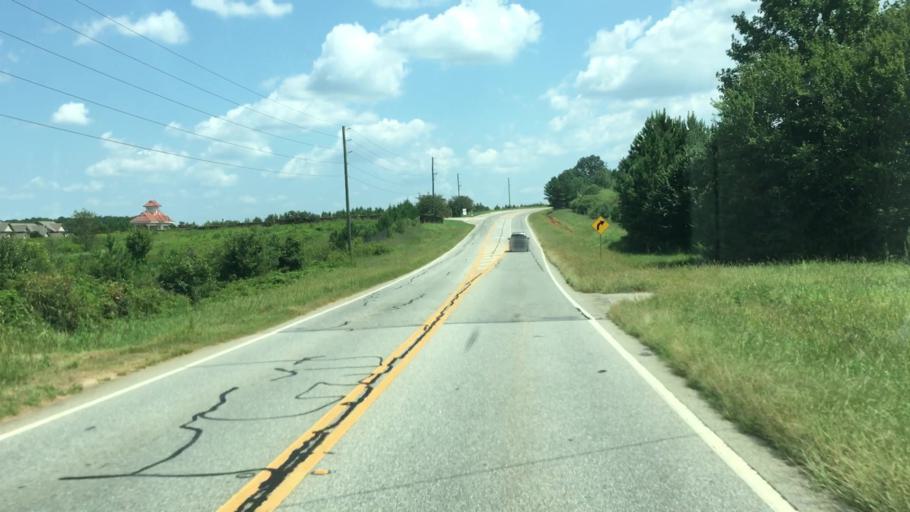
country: US
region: Georgia
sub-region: Barrow County
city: Statham
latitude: 33.9364
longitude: -83.6274
